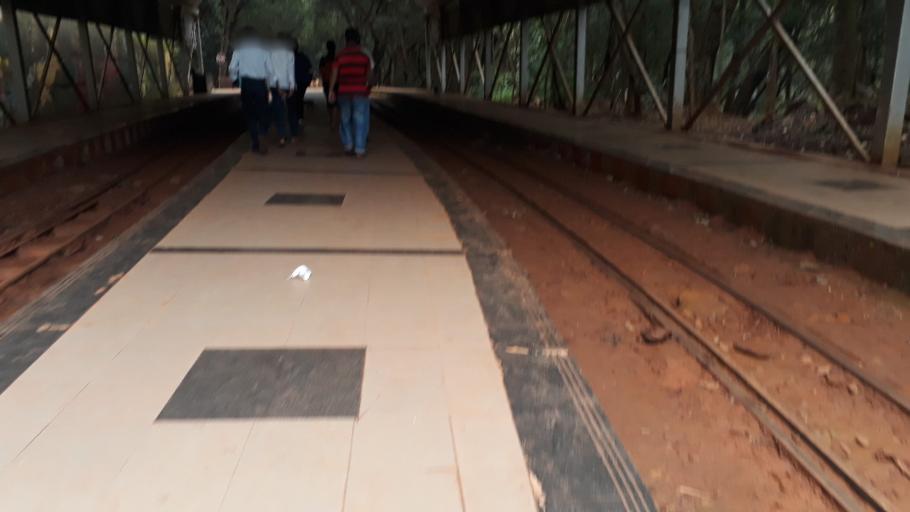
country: IN
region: Maharashtra
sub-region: Raigarh
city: Matheran
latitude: 19.0014
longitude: 73.2817
